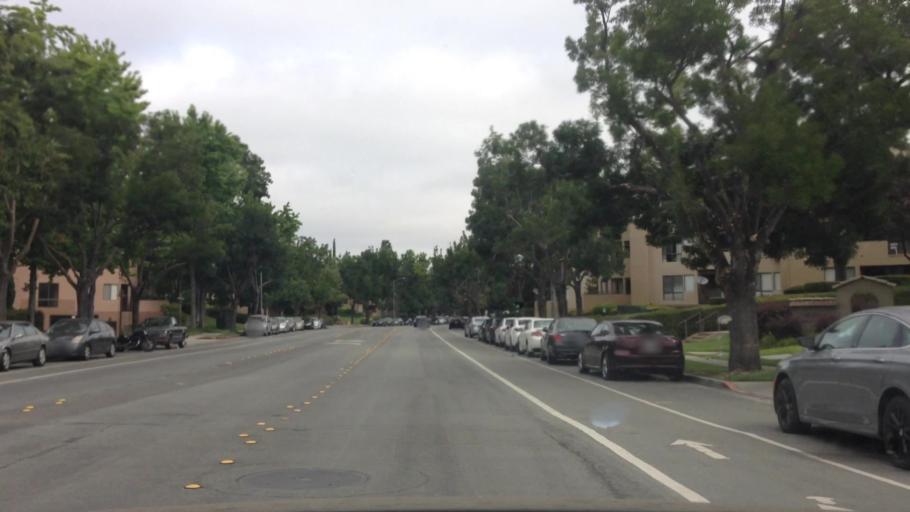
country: US
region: California
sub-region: Alameda County
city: Fremont
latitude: 37.5570
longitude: -121.9693
